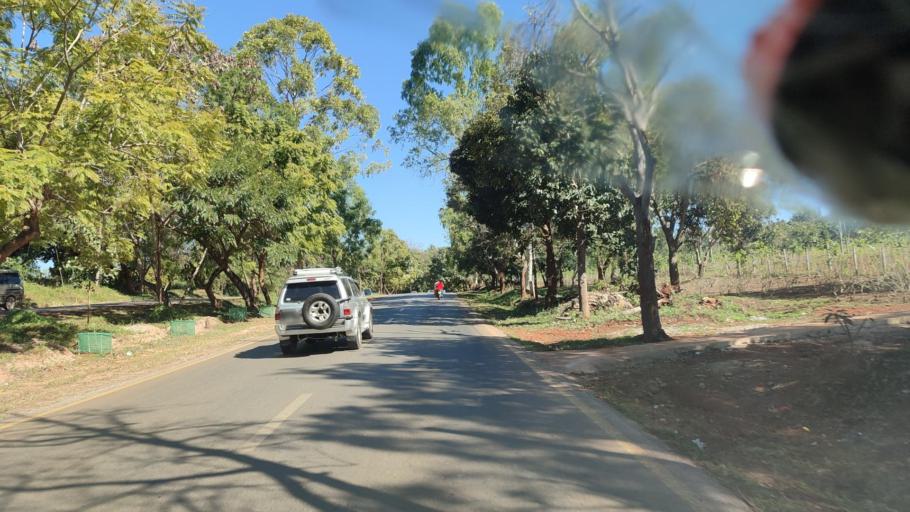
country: MM
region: Mandalay
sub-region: Pyin Oo Lwin District
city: Pyin Oo Lwin
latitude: 21.9882
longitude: 96.4191
